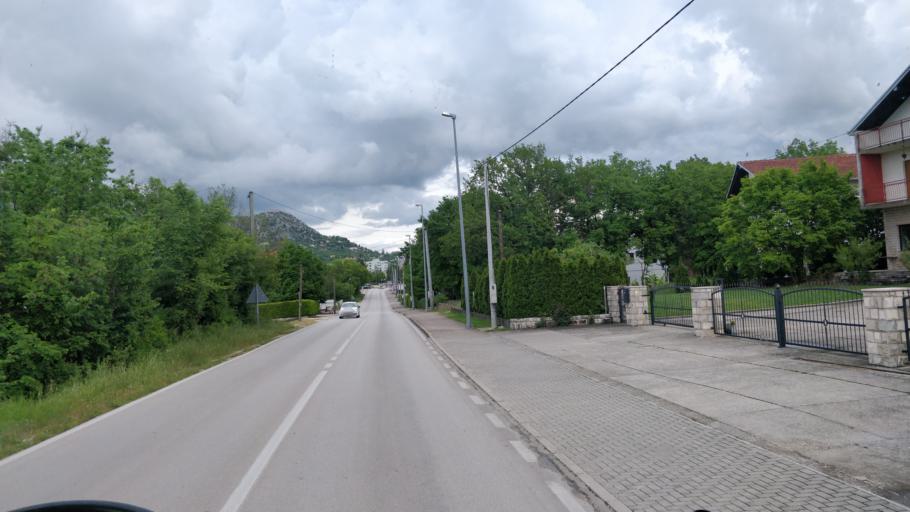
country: BA
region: Federation of Bosnia and Herzegovina
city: Ljubuski
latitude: 43.1895
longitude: 17.5309
